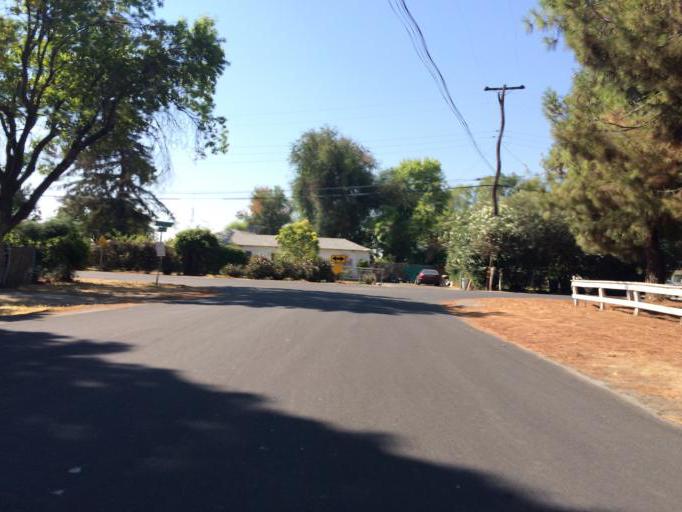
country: US
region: California
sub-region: Fresno County
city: Sunnyside
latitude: 36.7480
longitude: -119.7024
